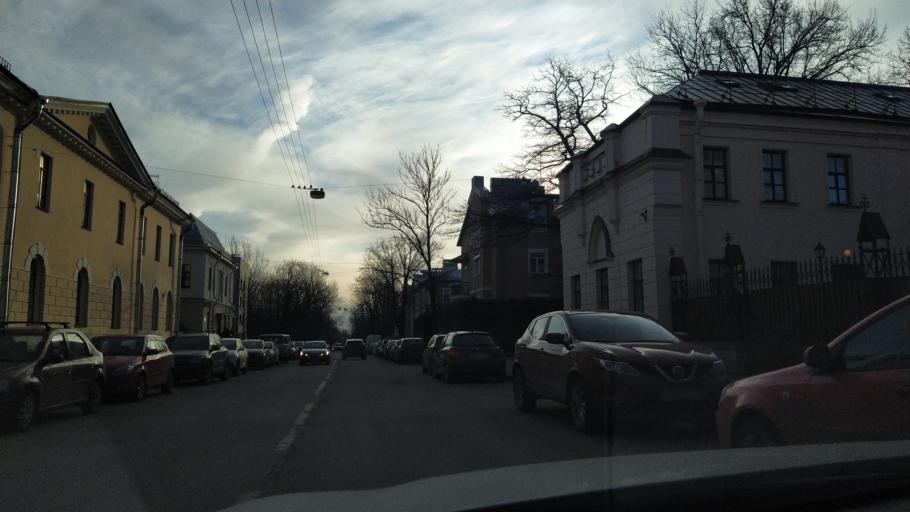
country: RU
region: St.-Petersburg
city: Pushkin
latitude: 59.7200
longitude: 30.3994
